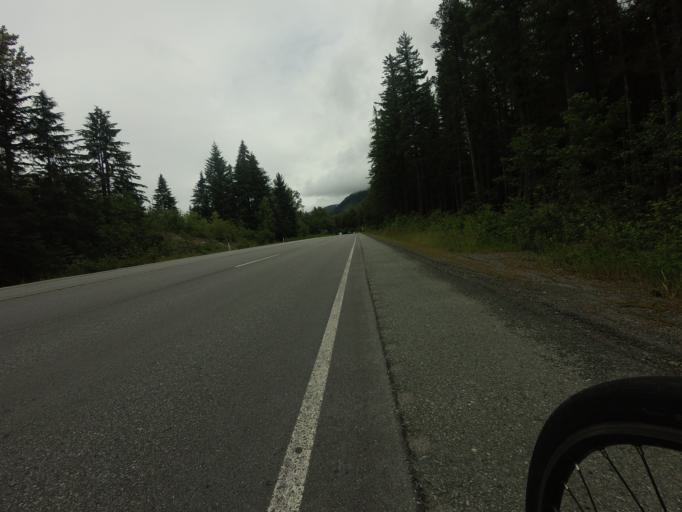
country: CA
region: British Columbia
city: Whistler
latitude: 49.9642
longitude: -123.1512
